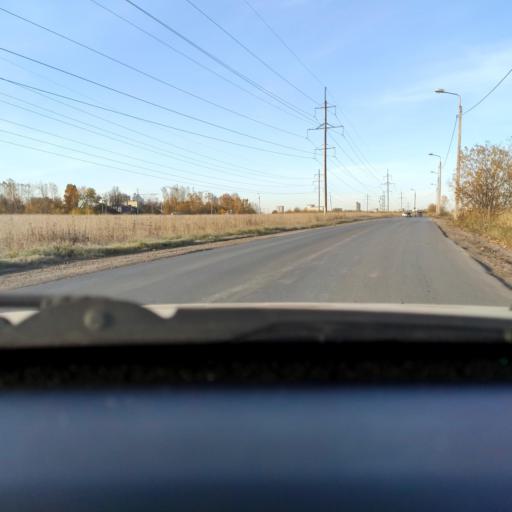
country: RU
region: Perm
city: Perm
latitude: 58.0191
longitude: 56.3370
